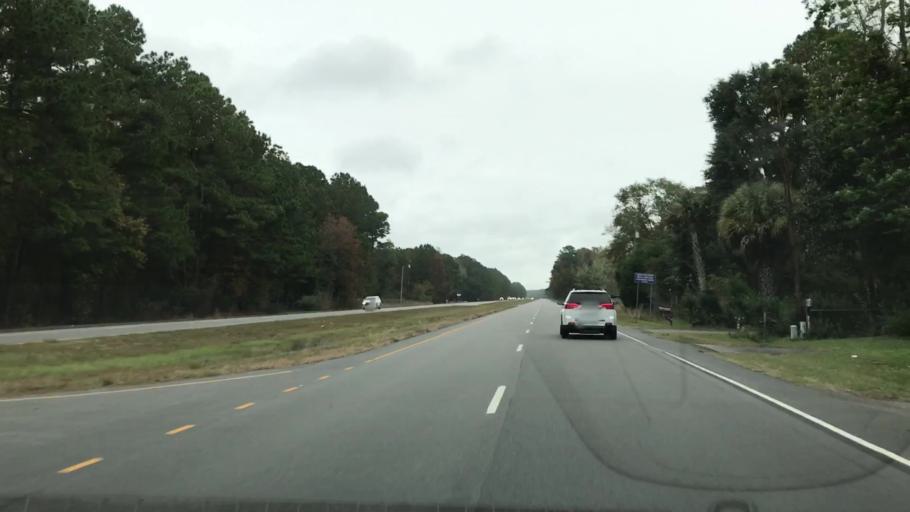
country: US
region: South Carolina
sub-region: Charleston County
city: Awendaw
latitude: 33.1091
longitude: -79.4614
